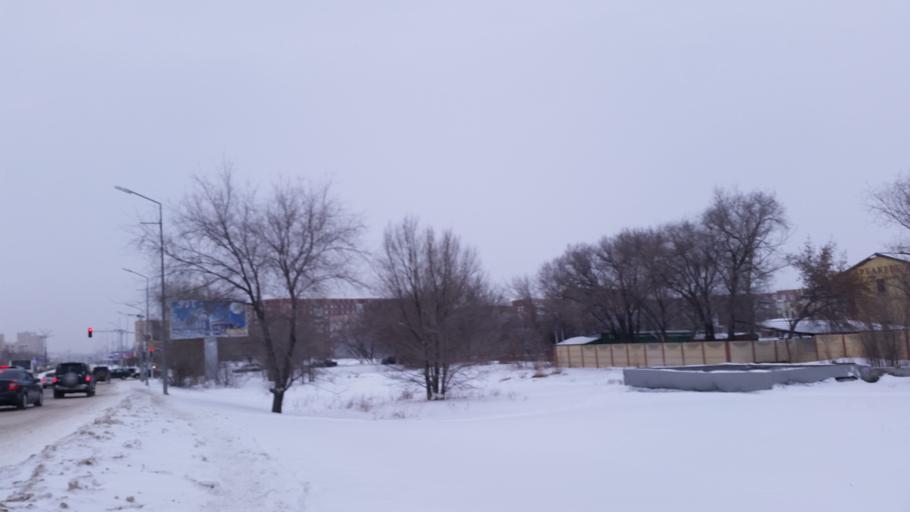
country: KZ
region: Qaraghandy
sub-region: Qaraghandy Qalasy
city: Karagandy
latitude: 49.7767
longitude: 73.1546
